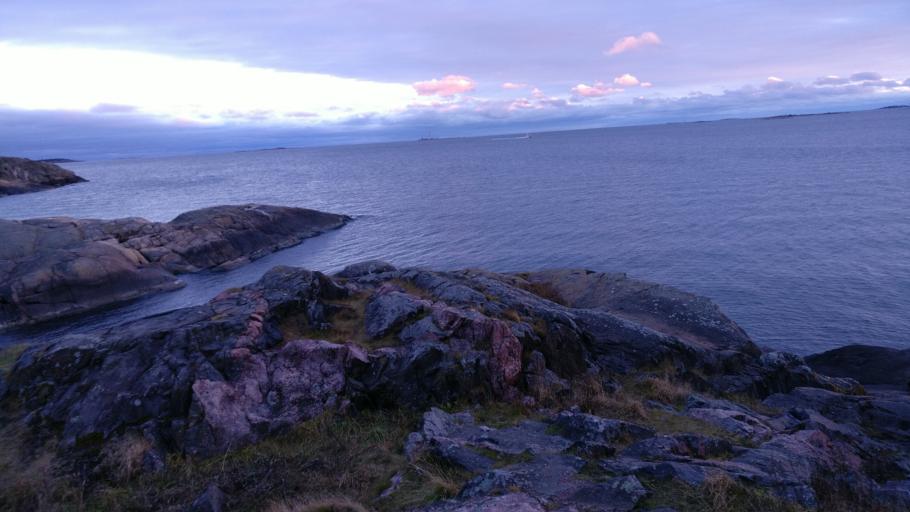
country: FI
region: Uusimaa
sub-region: Helsinki
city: Helsinki
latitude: 60.1419
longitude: 24.9818
